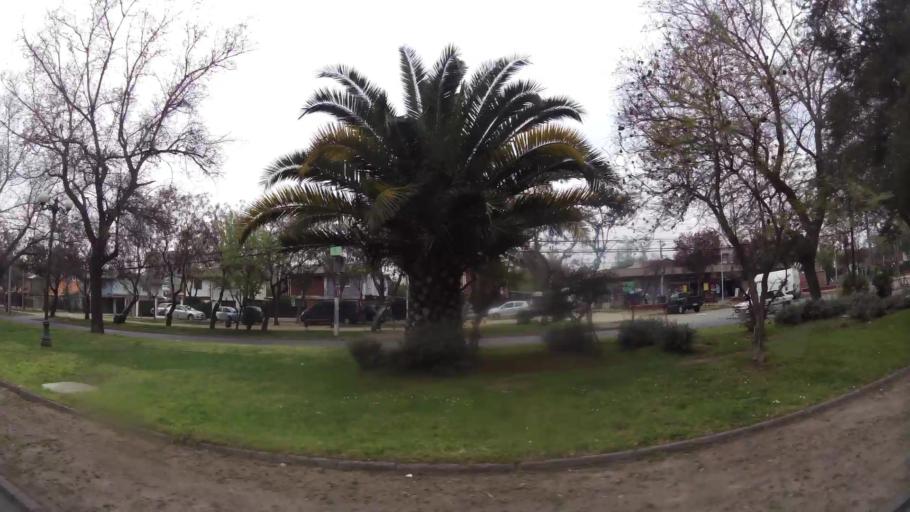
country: CL
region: Santiago Metropolitan
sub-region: Provincia de Santiago
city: Villa Presidente Frei, Nunoa, Santiago, Chile
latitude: -33.4737
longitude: -70.5955
